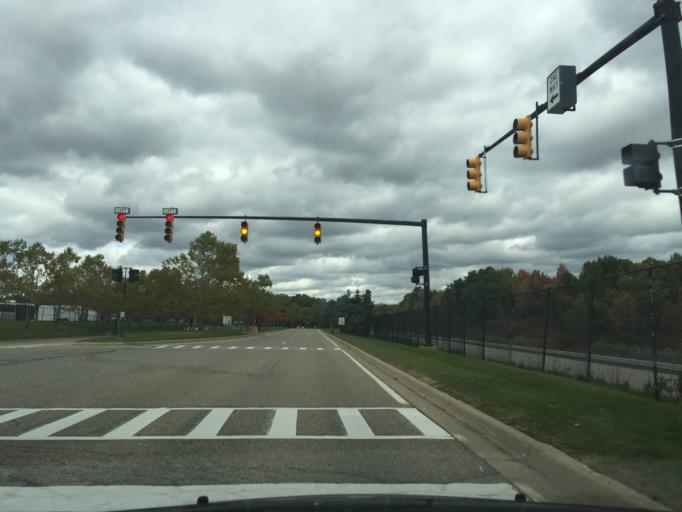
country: US
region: Michigan
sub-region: Oakland County
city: Auburn Hills
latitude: 42.6577
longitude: -83.2237
